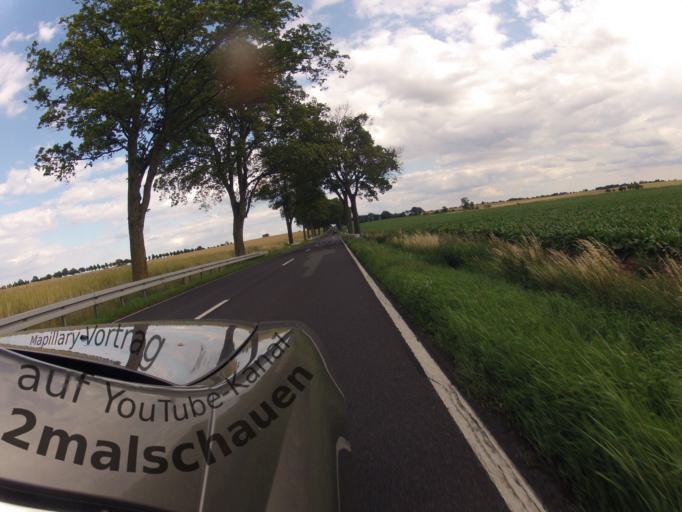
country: DE
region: Mecklenburg-Vorpommern
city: Seebad Bansin
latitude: 53.9012
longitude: 14.0516
